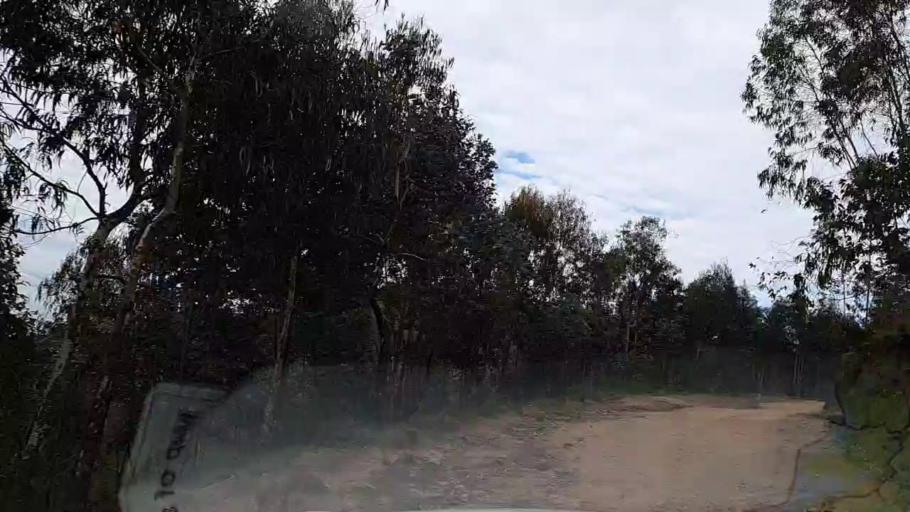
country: RW
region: Southern Province
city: Nzega
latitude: -2.4086
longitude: 29.4913
